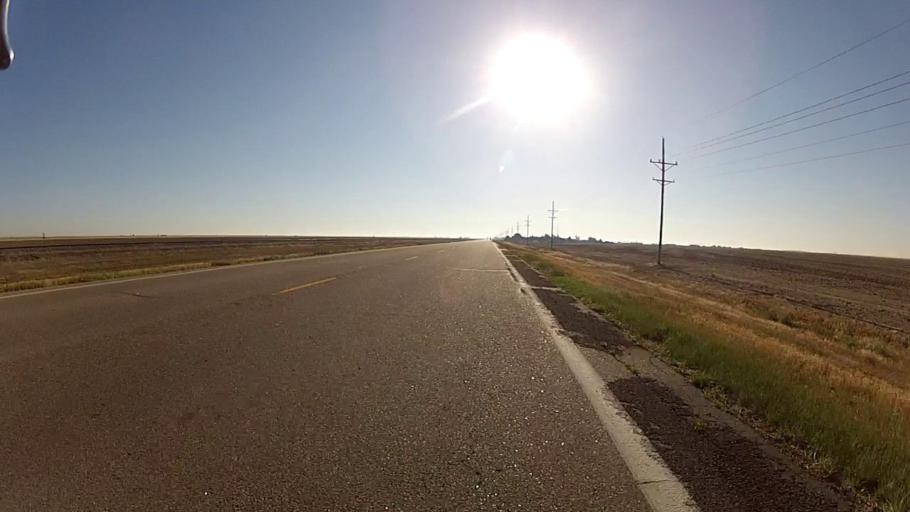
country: US
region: Kansas
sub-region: Haskell County
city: Sublette
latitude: 37.4916
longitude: -100.8143
